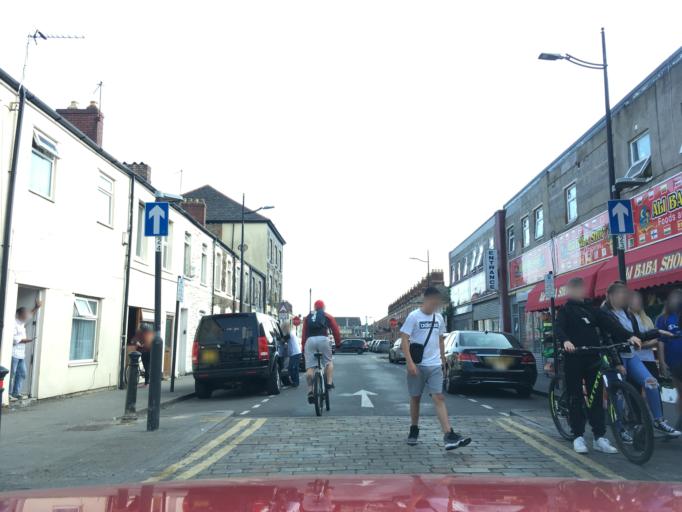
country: GB
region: Wales
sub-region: Cardiff
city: Cardiff
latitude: 51.4844
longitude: -3.1567
